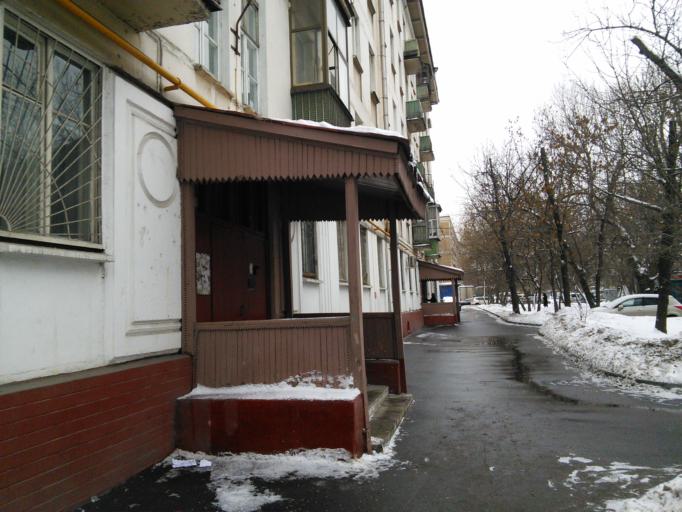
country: RU
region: Moscow
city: Mar'ina Roshcha
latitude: 55.7955
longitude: 37.6156
